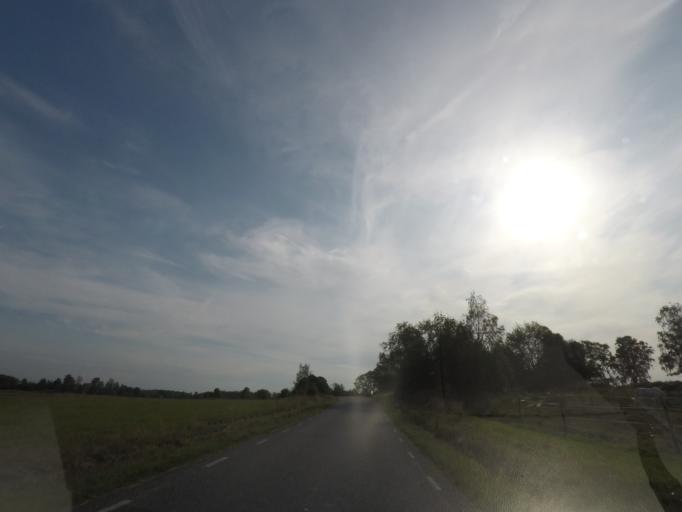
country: SE
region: Vaestmanland
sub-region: Hallstahammars Kommun
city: Kolback
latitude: 59.5286
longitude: 16.1426
